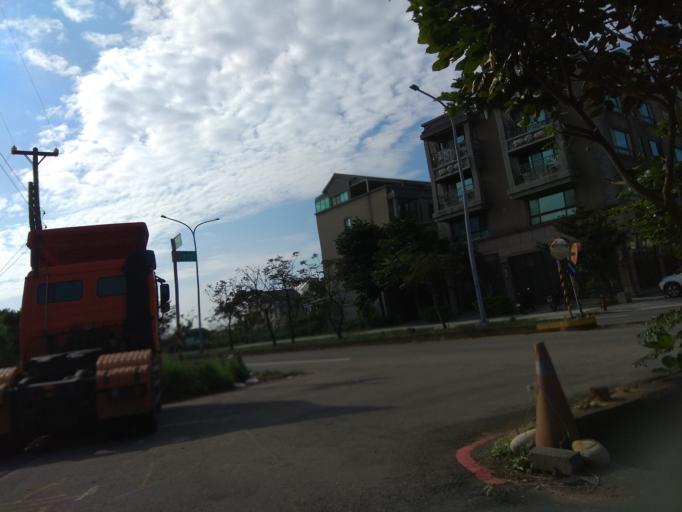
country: TW
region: Taiwan
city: Taoyuan City
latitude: 25.0506
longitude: 121.1769
